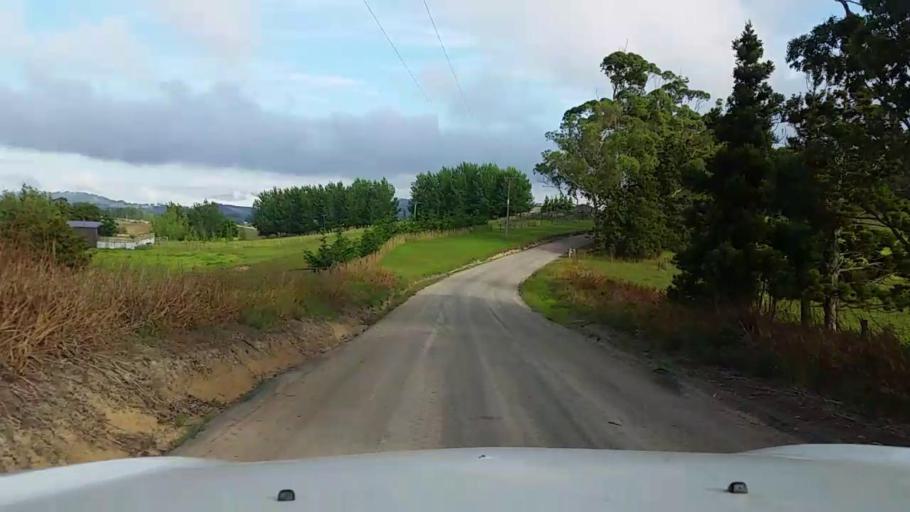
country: NZ
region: Northland
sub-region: Whangarei
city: Maungatapere
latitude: -35.6733
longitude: 174.1760
